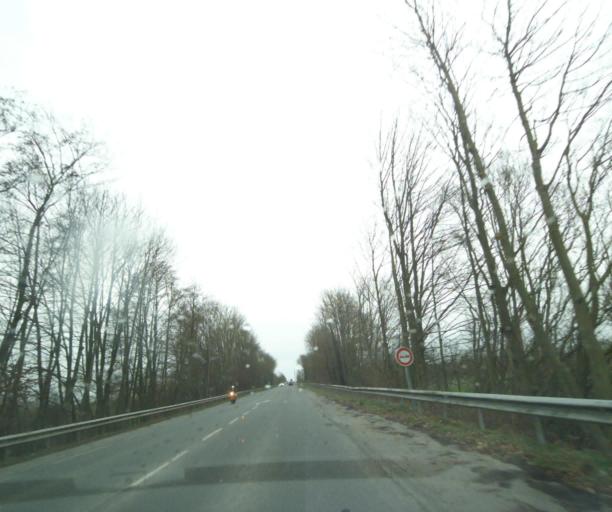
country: FR
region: Nord-Pas-de-Calais
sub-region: Departement du Nord
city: Escautpont
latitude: 50.4153
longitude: 3.5678
